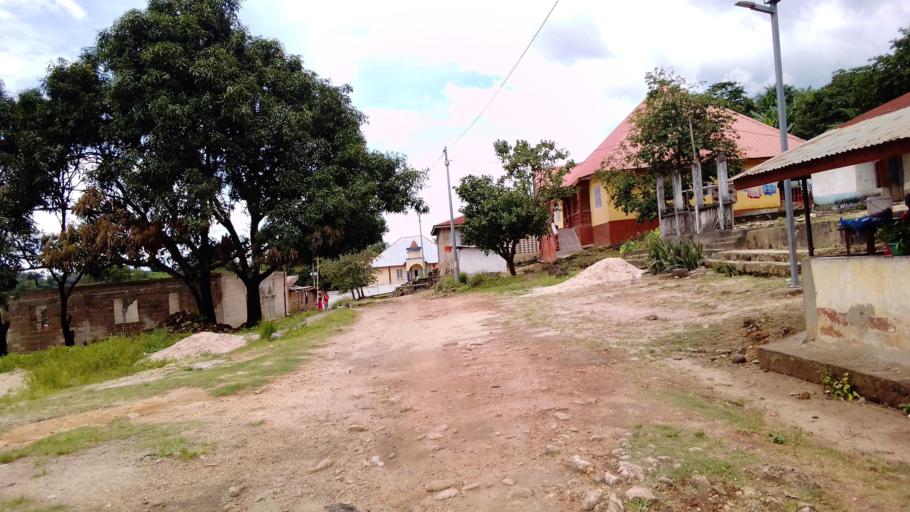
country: SL
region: Eastern Province
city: Koyima
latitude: 8.6996
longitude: -11.0089
